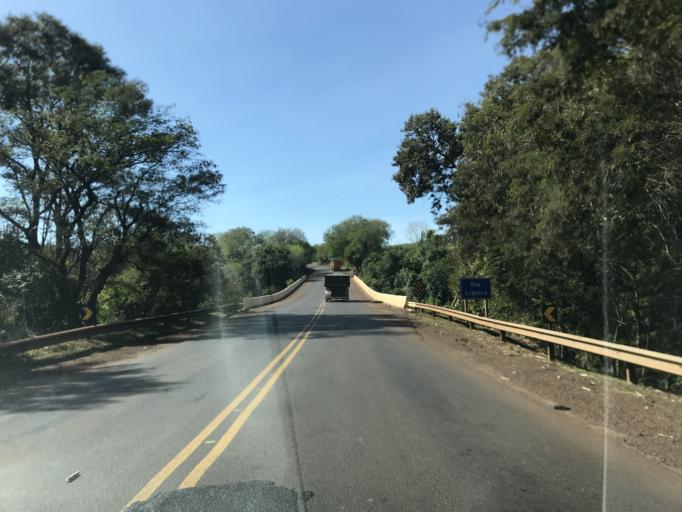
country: BR
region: Parana
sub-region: Cianorte
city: Cianorte
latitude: -23.6565
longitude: -52.5078
